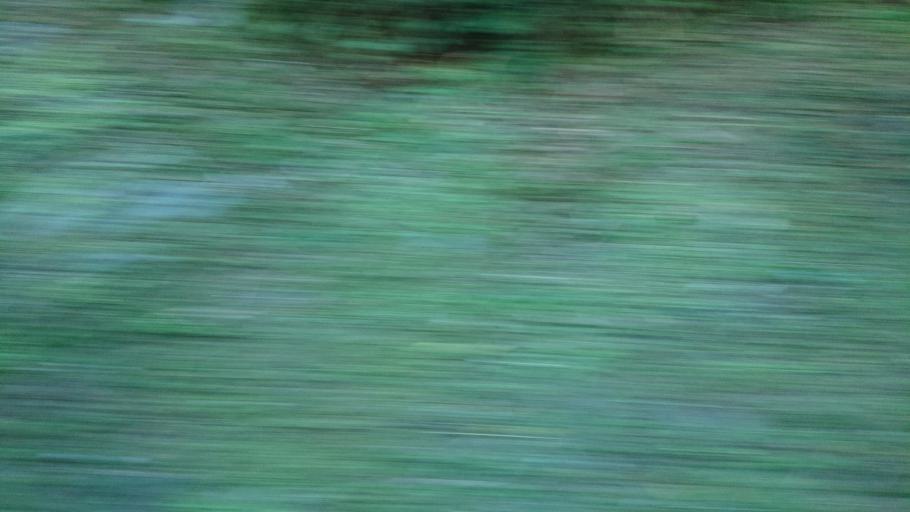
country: TW
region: Taiwan
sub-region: Yilan
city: Yilan
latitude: 24.5787
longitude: 121.4864
